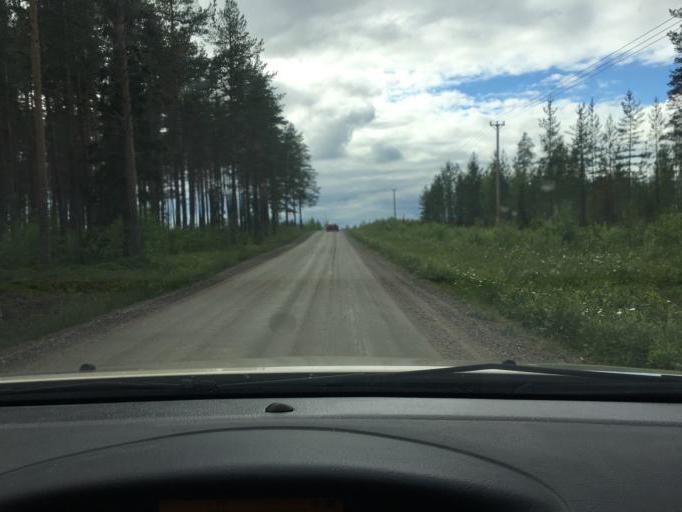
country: SE
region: Norrbotten
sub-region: Overkalix Kommun
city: OEverkalix
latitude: 66.0896
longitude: 22.8370
